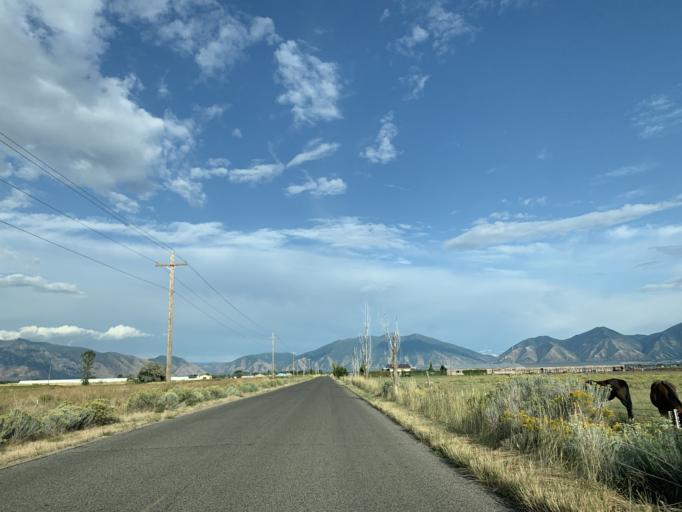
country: US
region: Utah
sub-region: Utah County
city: West Mountain
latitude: 40.1142
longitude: -111.7913
